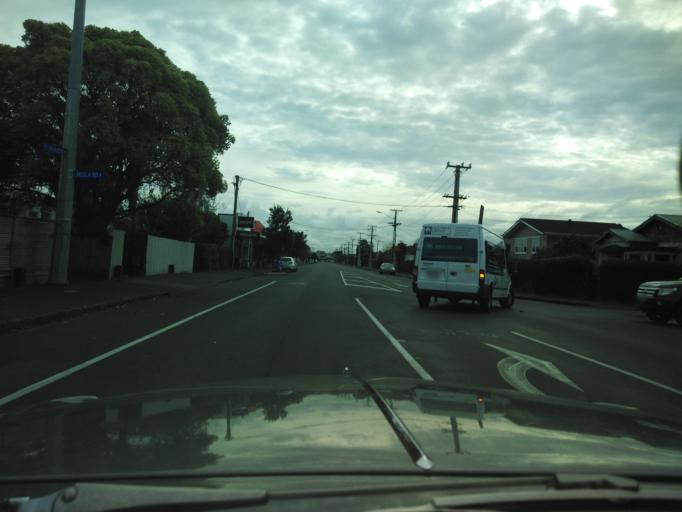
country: NZ
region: Auckland
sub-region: Auckland
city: Rosebank
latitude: -36.8640
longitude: 174.7054
